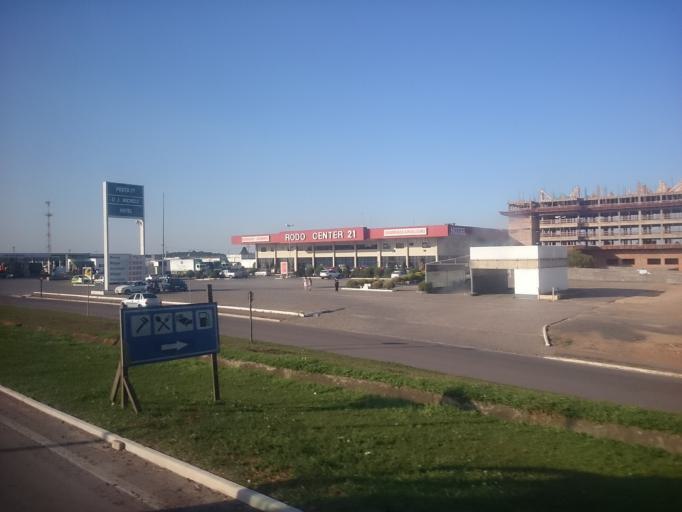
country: BR
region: Parana
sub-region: Araucaria
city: Araucaria
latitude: -25.6440
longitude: -49.3127
